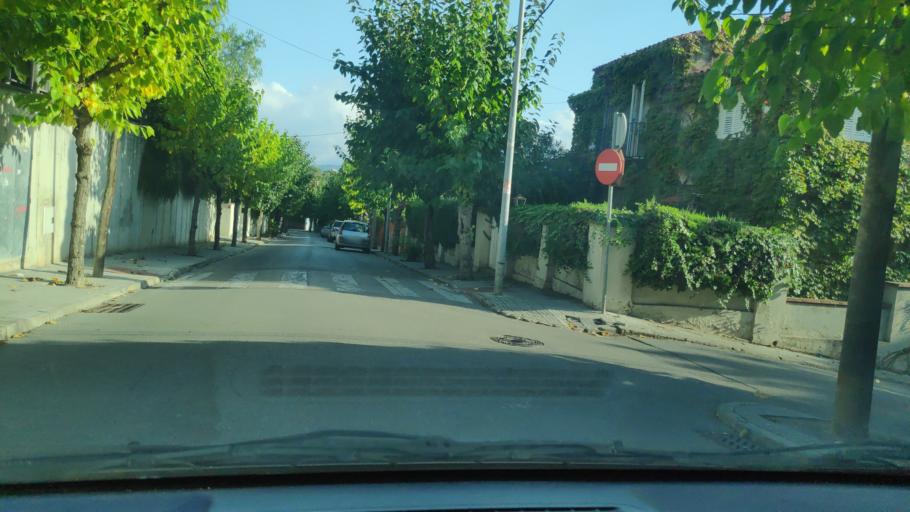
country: ES
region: Catalonia
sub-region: Provincia de Barcelona
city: Sant Quirze del Valles
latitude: 41.5021
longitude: 2.0864
